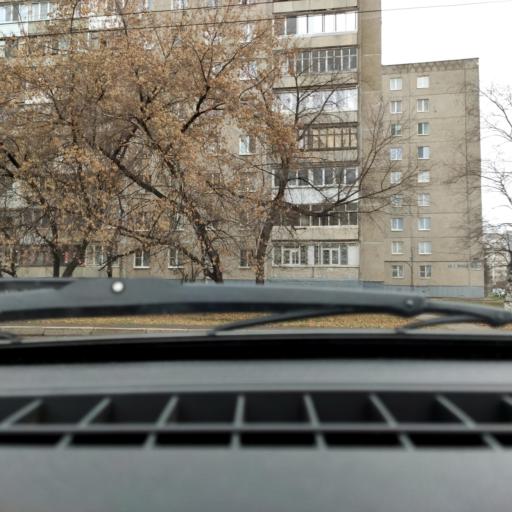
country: RU
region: Bashkortostan
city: Ufa
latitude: 54.7767
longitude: 56.1243
